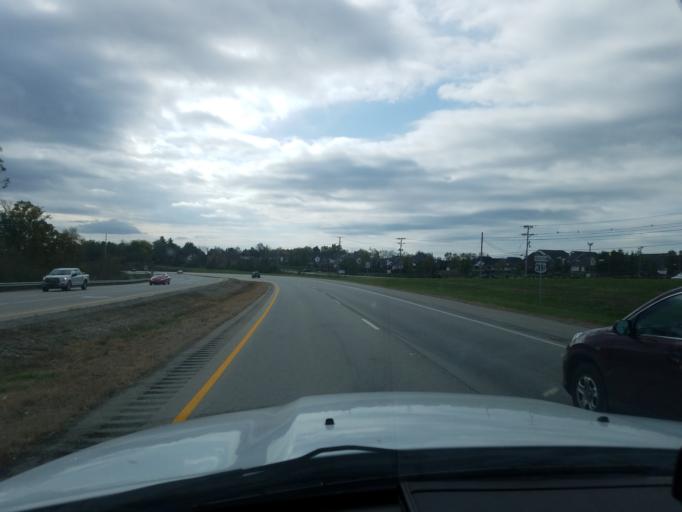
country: US
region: Kentucky
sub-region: Bullitt County
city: Mount Washington
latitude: 38.1003
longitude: -85.5658
